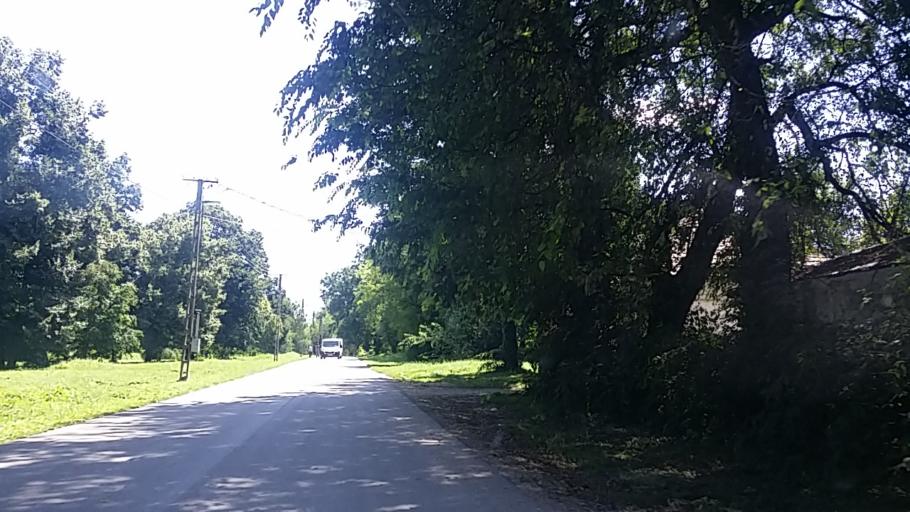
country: HU
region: Fejer
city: Deg
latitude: 46.8736
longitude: 18.4414
